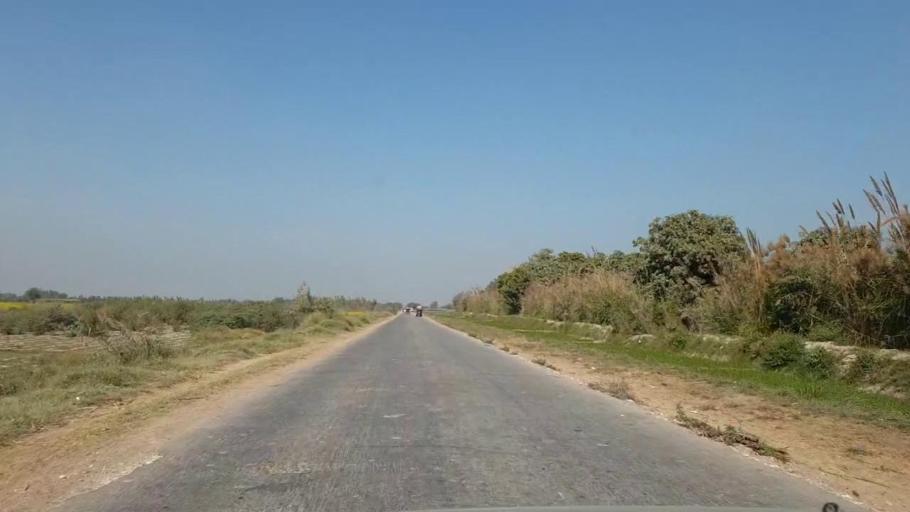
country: PK
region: Sindh
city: Tando Adam
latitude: 25.6527
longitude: 68.5886
